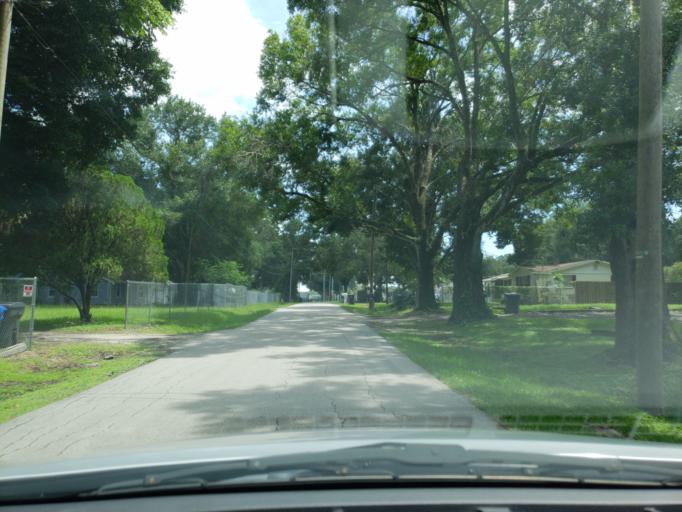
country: US
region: Florida
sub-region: Hillsborough County
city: East Lake-Orient Park
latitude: 27.9683
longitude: -82.3709
